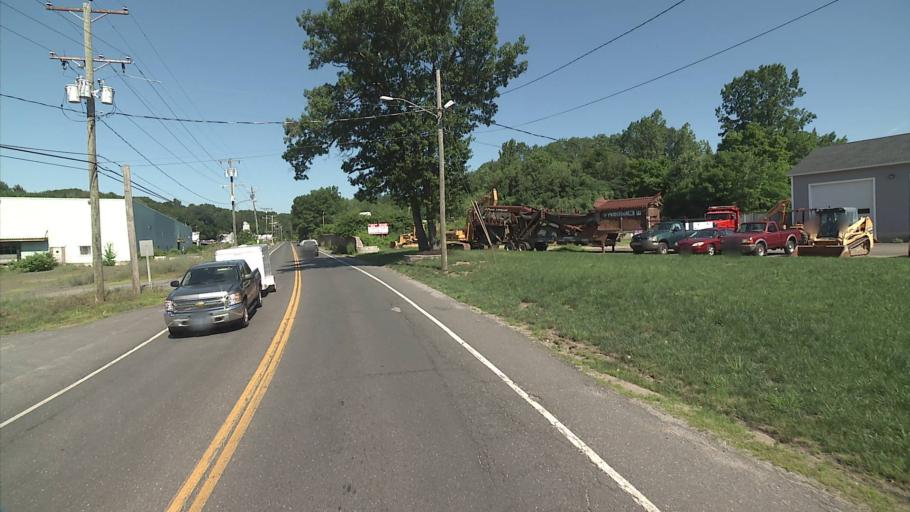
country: US
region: Connecticut
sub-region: Litchfield County
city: Terryville
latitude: 41.6731
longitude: -72.9935
